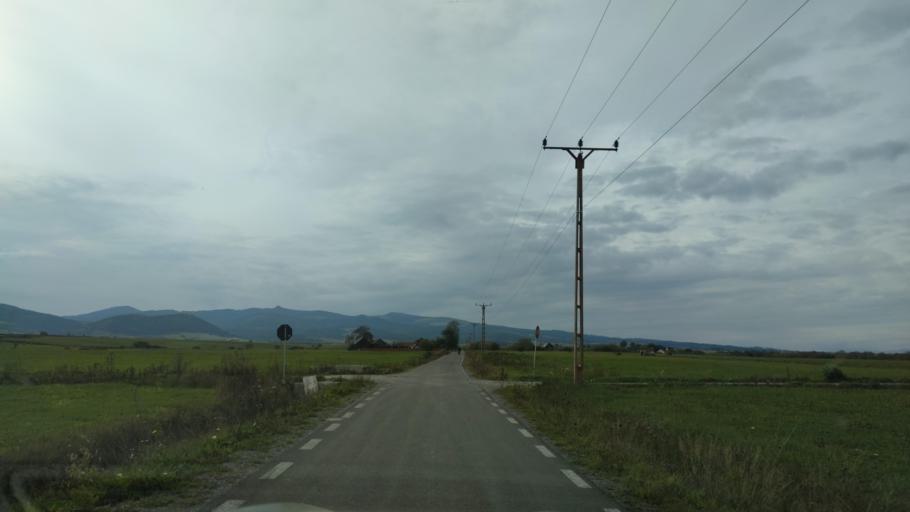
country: RO
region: Harghita
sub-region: Comuna Remetea
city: Remetea
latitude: 46.8080
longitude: 25.4321
